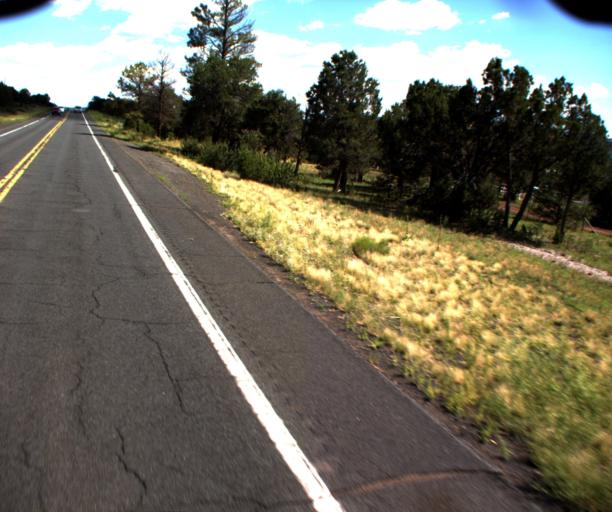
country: US
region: Arizona
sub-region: Coconino County
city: Williams
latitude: 35.3423
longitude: -112.1648
